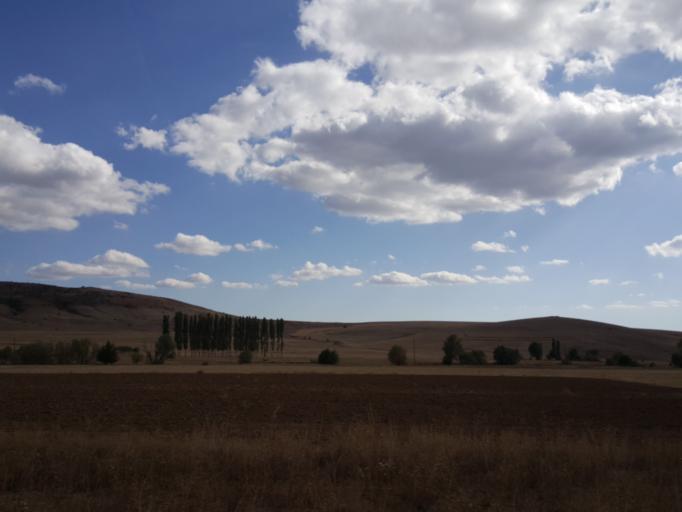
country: TR
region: Tokat
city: Sulusaray
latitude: 39.9859
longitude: 35.9468
